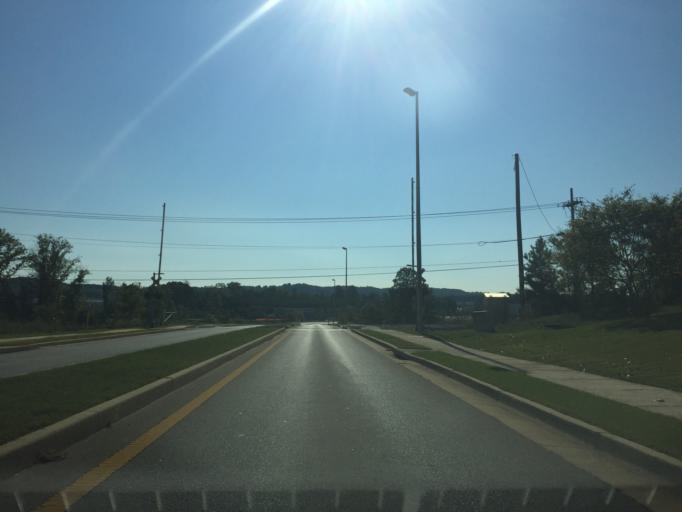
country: US
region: Tennessee
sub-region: Hamilton County
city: Harrison
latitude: 35.0751
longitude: -85.1487
